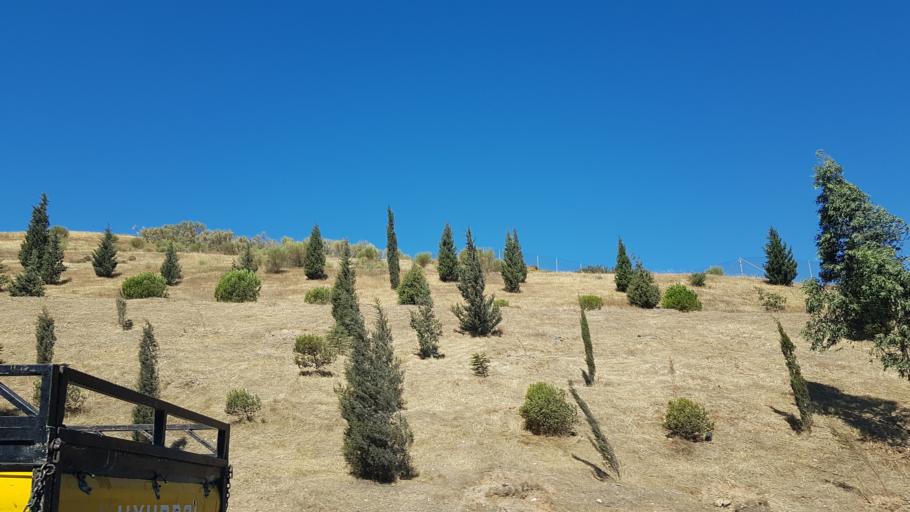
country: TR
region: Izmir
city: Buca
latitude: 38.4008
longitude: 27.2298
